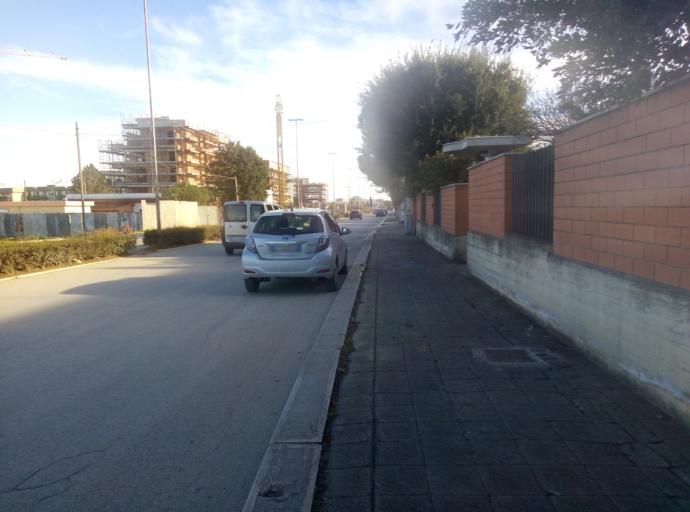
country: IT
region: Apulia
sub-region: Provincia di Bari
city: Ruvo di Puglia
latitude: 41.1212
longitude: 16.4906
